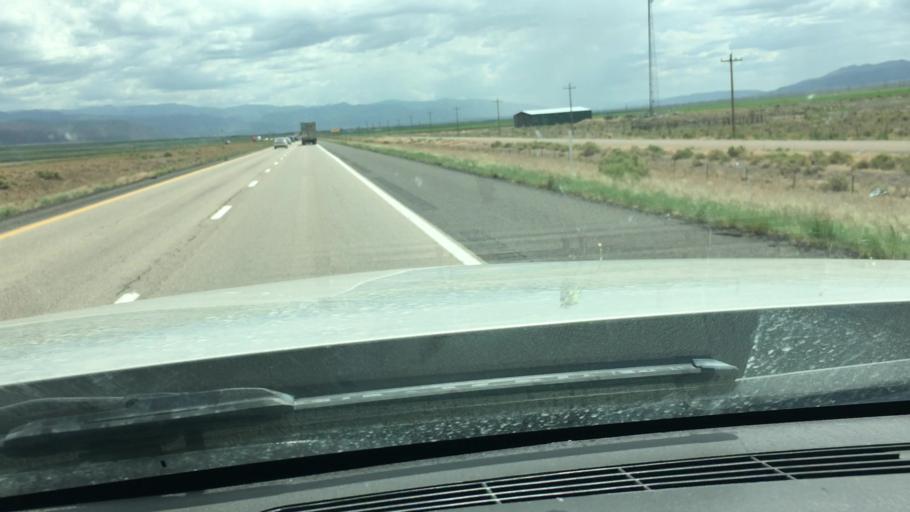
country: US
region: Utah
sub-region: Beaver County
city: Beaver
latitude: 38.0545
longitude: -112.6982
